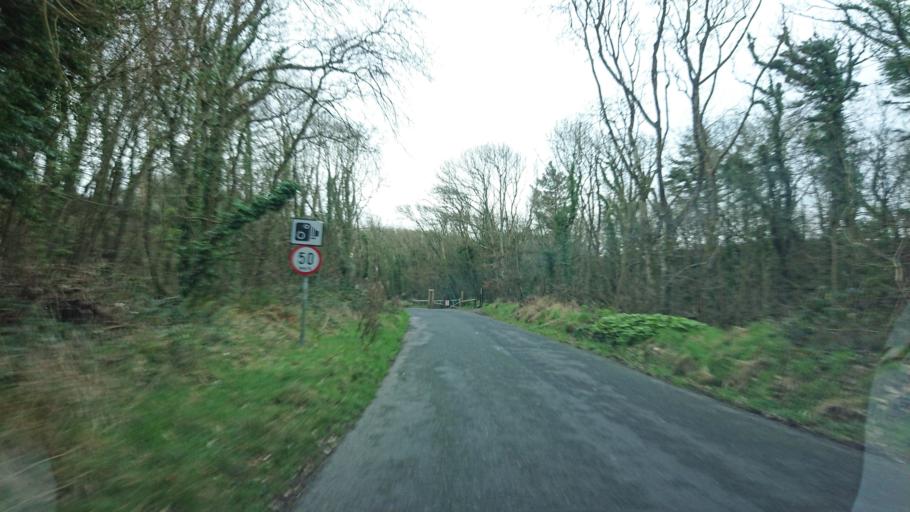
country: IE
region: Munster
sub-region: Waterford
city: Tra Mhor
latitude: 52.1443
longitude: -7.1715
